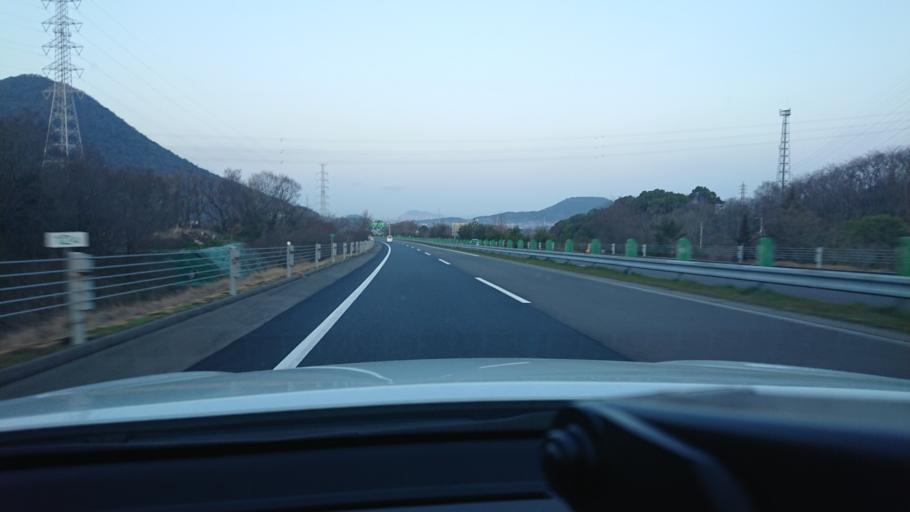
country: JP
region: Kagawa
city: Sakaidecho
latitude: 34.2809
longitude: 133.8687
